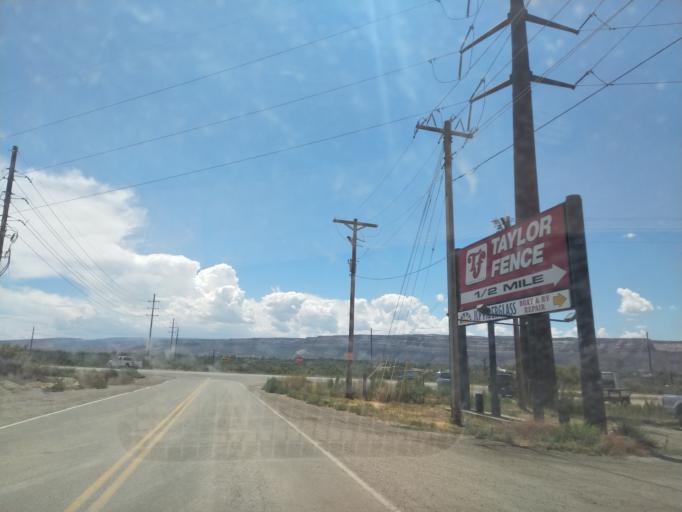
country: US
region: Colorado
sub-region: Mesa County
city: Redlands
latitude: 39.1159
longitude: -108.6546
